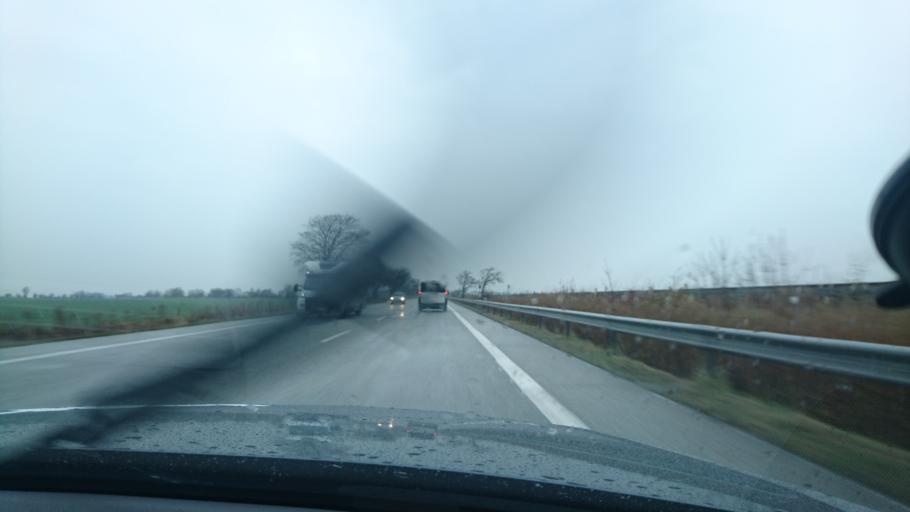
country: DE
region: Schleswig-Holstein
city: Fehmarn
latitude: 54.4372
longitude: 11.1537
